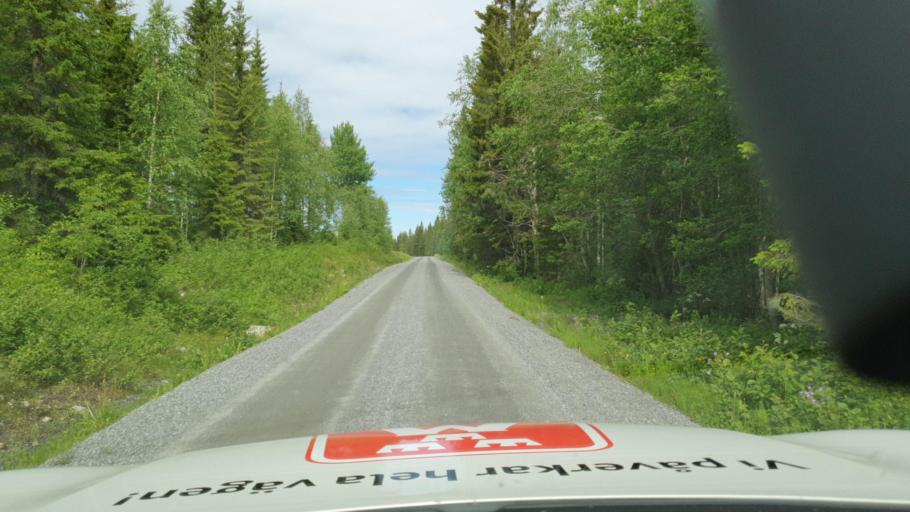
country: SE
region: Vaesterbotten
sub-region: Skelleftea Kommun
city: Langsele
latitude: 64.6222
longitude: 20.2618
